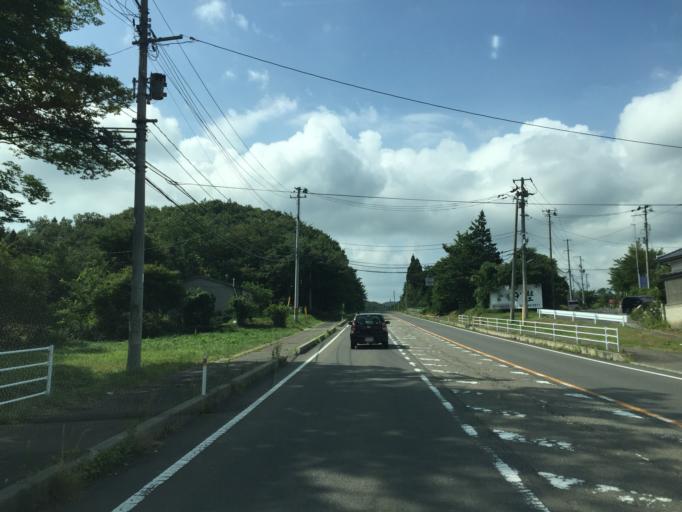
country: JP
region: Fukushima
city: Motomiya
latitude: 37.4957
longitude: 140.2803
